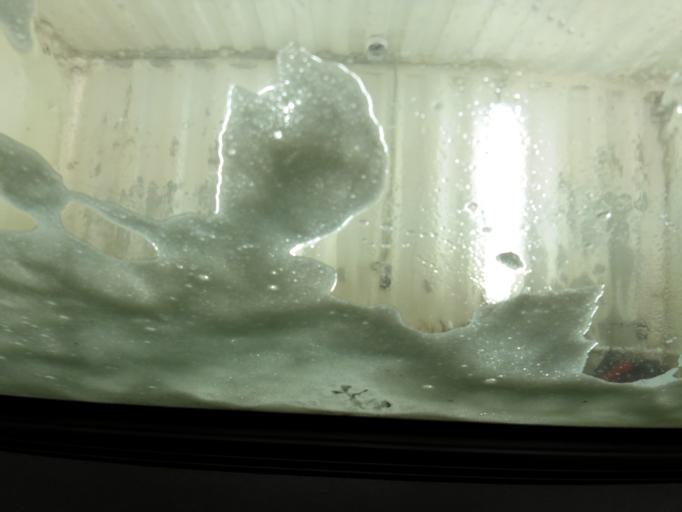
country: RU
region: Sverdlovsk
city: Shirokaya Rechka
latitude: 56.7982
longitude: 60.4932
